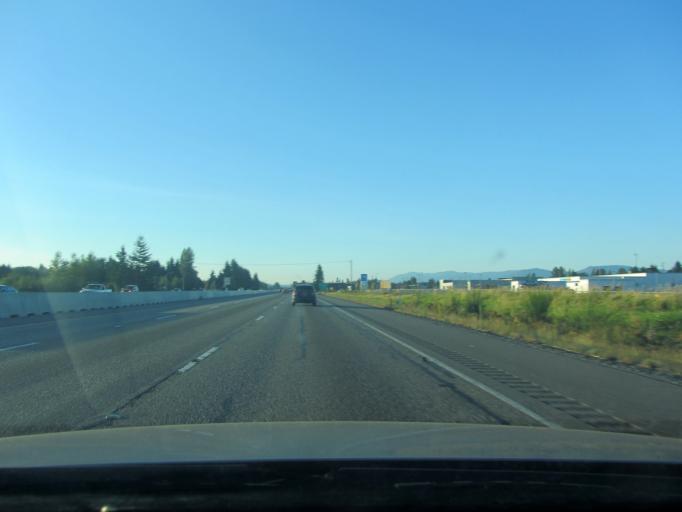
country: US
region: Washington
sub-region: Snohomish County
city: Smokey Point
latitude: 48.1380
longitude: -122.1861
